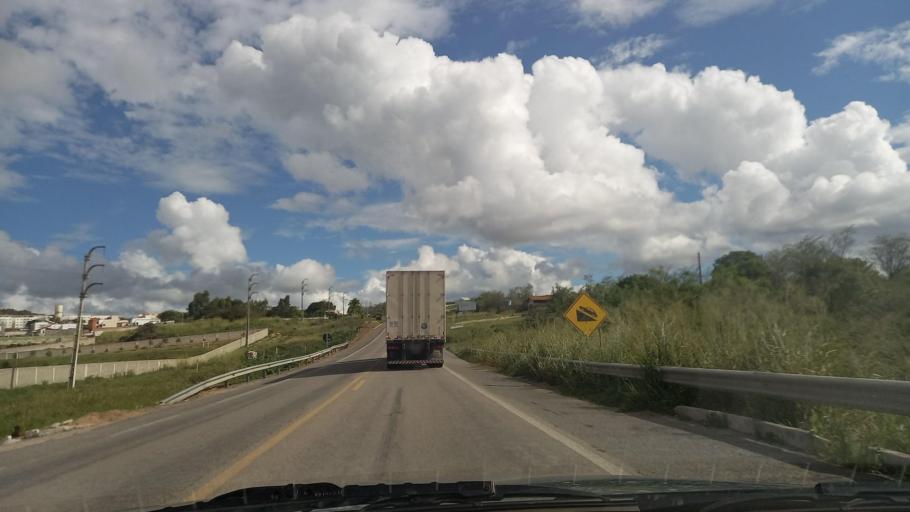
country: BR
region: Pernambuco
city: Garanhuns
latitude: -8.8519
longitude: -36.4620
